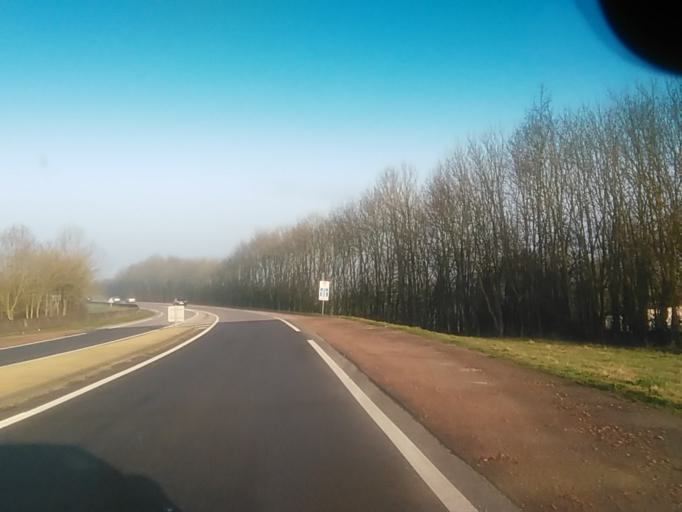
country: FR
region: Lower Normandy
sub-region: Departement du Calvados
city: Falaise
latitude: 48.8824
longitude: -0.2070
